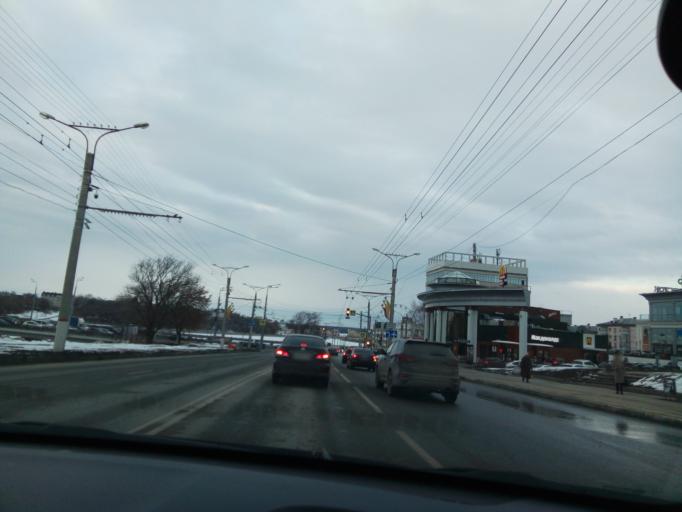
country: RU
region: Chuvashia
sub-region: Cheboksarskiy Rayon
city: Cheboksary
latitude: 56.1430
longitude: 47.2458
